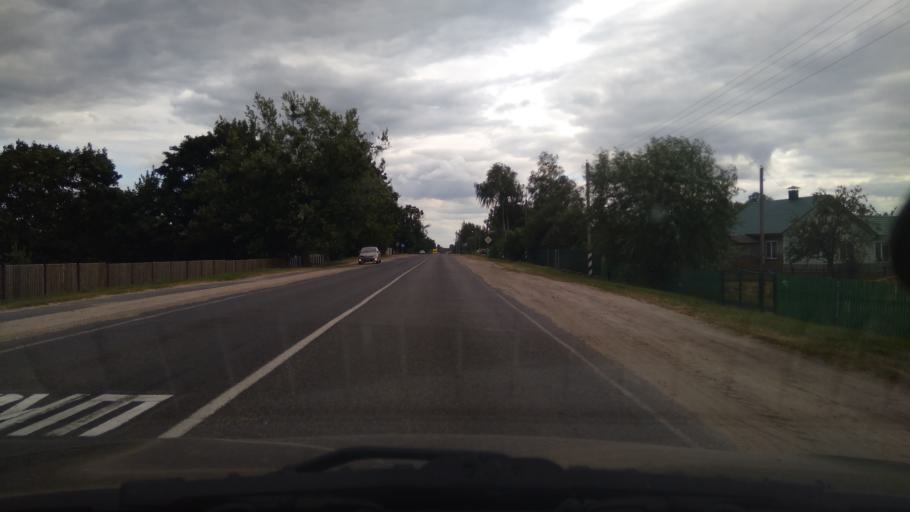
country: BY
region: Brest
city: Byelaazyorsk
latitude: 52.4997
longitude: 25.1904
